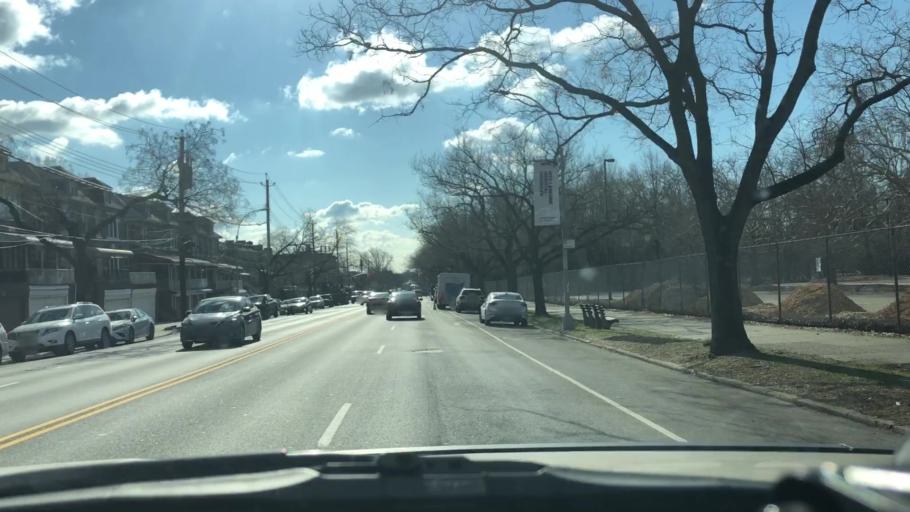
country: US
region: New York
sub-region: Kings County
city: Bensonhurst
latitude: 40.6164
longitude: -74.0178
